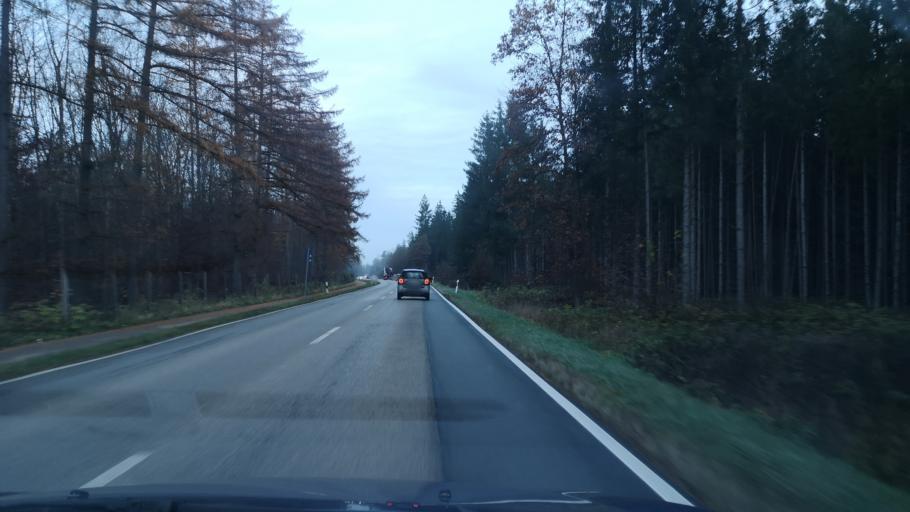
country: DE
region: Bavaria
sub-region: Upper Bavaria
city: Forstinning
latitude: 48.1467
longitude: 11.9206
